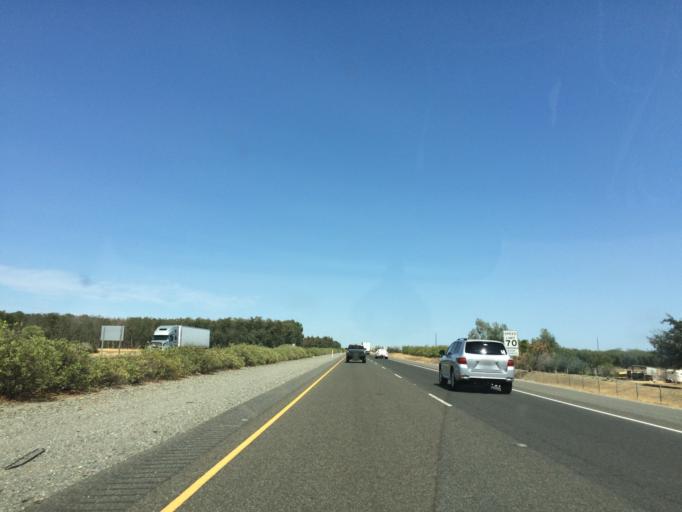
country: US
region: California
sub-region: Glenn County
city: Orland
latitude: 39.7583
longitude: -122.2053
